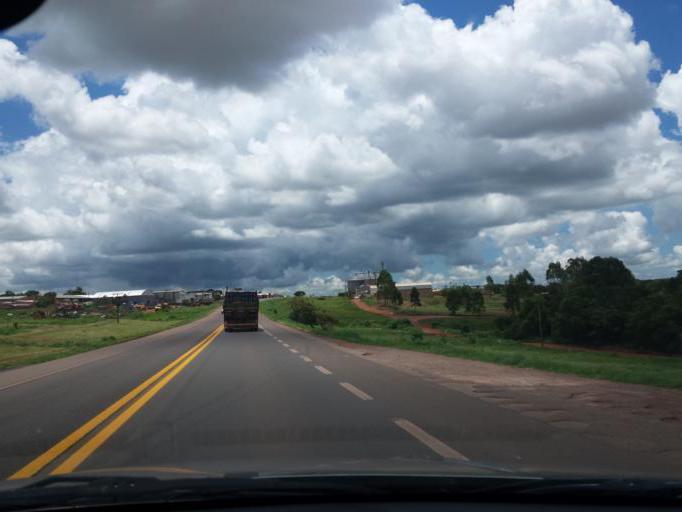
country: BR
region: Goias
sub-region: Cristalina
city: Cristalina
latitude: -16.7716
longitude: -47.6203
